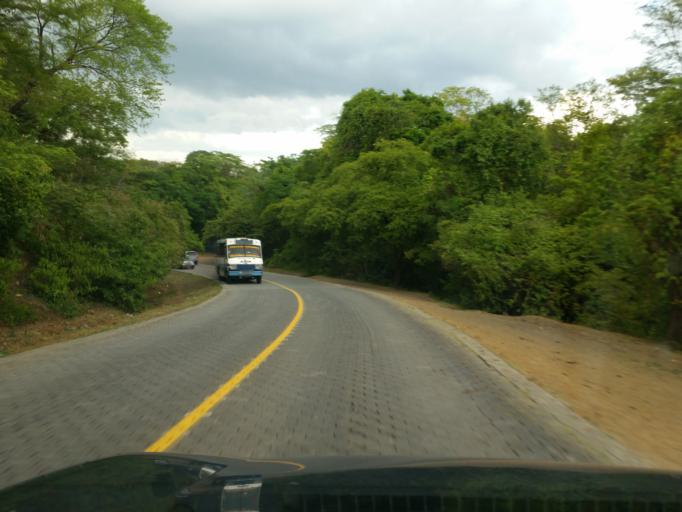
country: NI
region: Managua
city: Carlos Fonseca Amador
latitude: 11.9009
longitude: -86.5109
